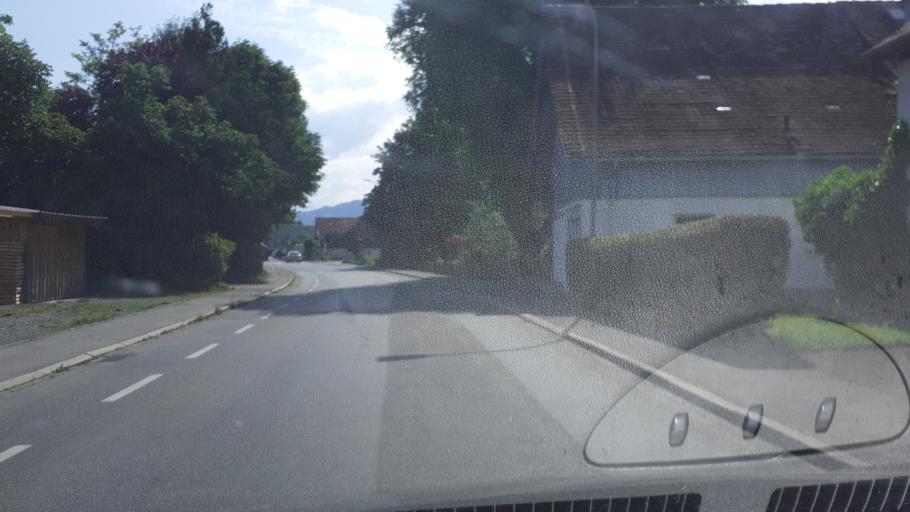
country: AT
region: Vorarlberg
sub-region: Politischer Bezirk Dornbirn
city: Lustenau
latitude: 47.4183
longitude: 9.6584
